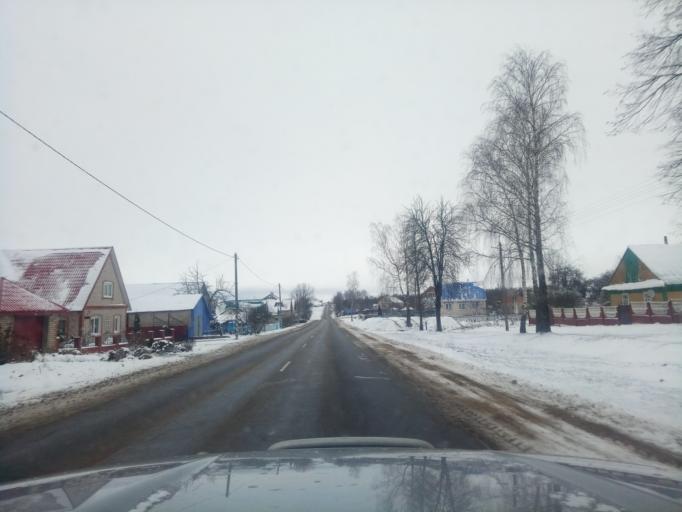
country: BY
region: Minsk
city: Kapyl'
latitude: 53.1588
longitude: 27.0957
